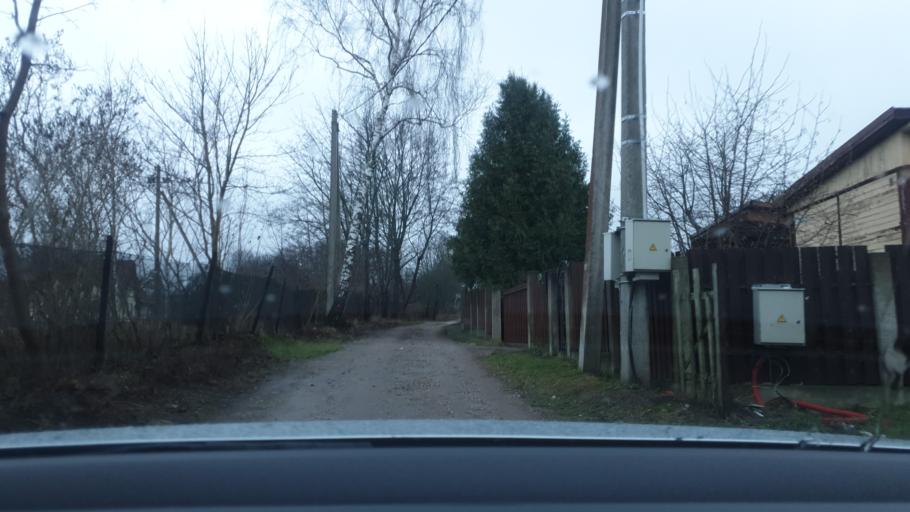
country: LT
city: Skaidiskes
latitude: 54.7032
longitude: 25.4038
